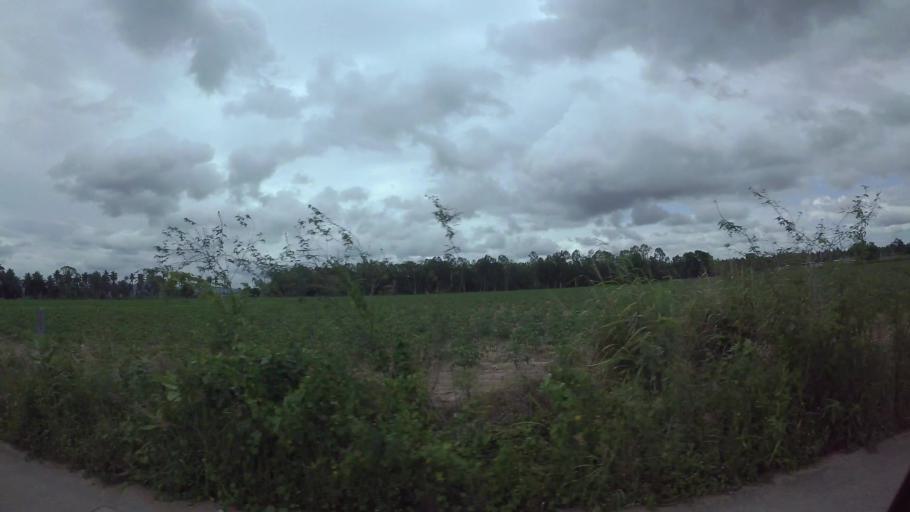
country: TH
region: Chon Buri
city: Si Racha
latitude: 13.1789
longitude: 100.9806
